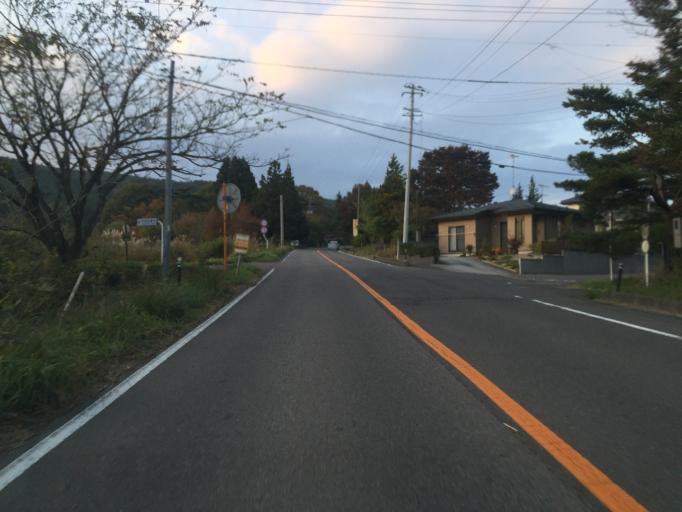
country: JP
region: Fukushima
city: Nihommatsu
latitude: 37.5977
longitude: 140.3563
